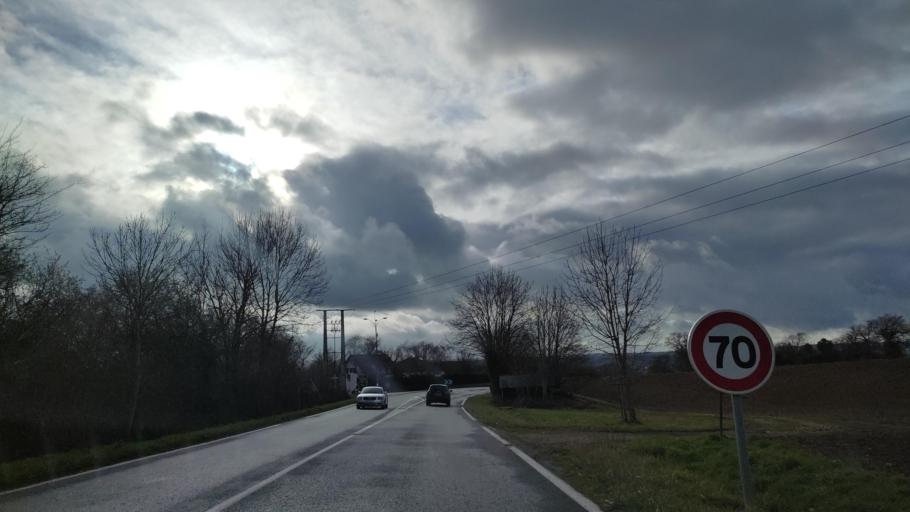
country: FR
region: Limousin
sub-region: Departement de la Haute-Vienne
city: Aixe-sur-Vienne
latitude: 45.8095
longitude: 1.1632
